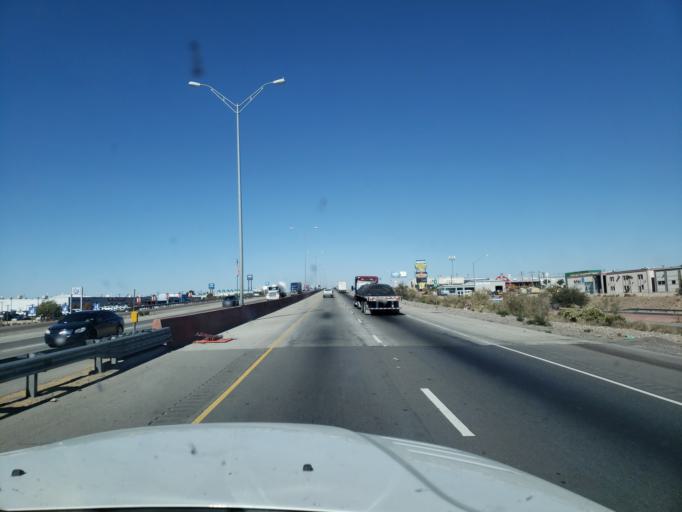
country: US
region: New Mexico
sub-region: Dona Ana County
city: Sunland Park
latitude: 31.8561
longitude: -106.5753
